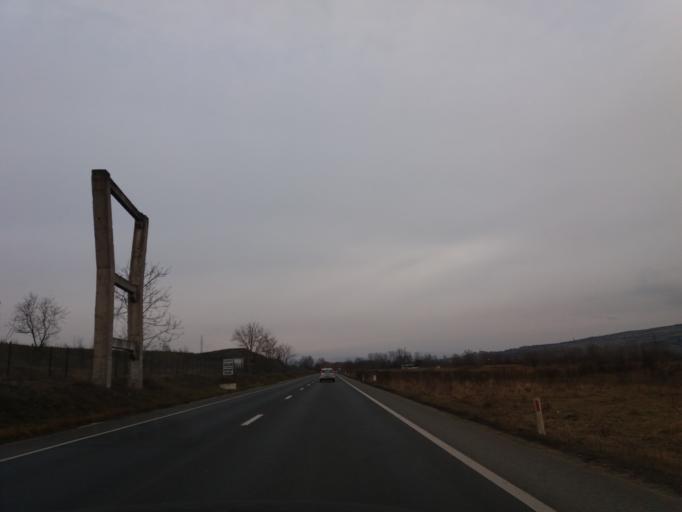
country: RO
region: Hunedoara
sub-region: Comuna Calan
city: Calan
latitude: 45.7455
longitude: 23.0000
